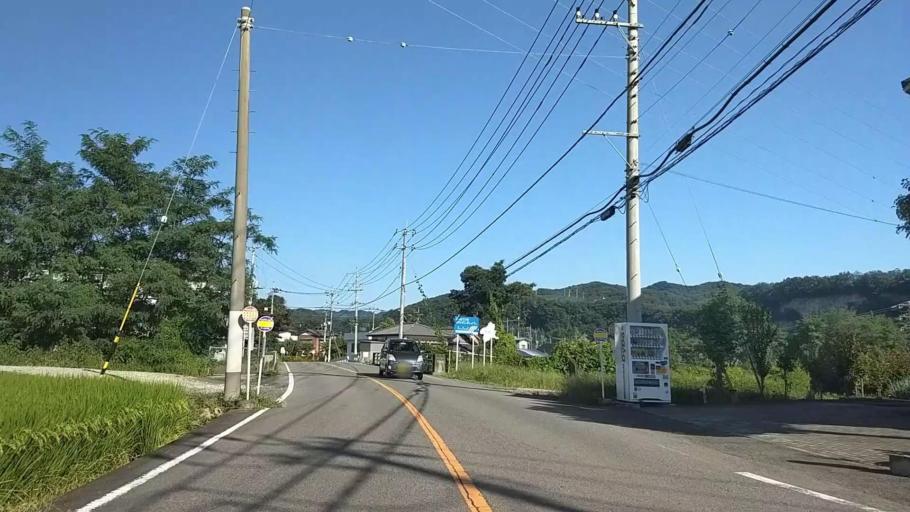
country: JP
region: Gunma
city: Annaka
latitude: 36.3333
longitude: 138.9223
